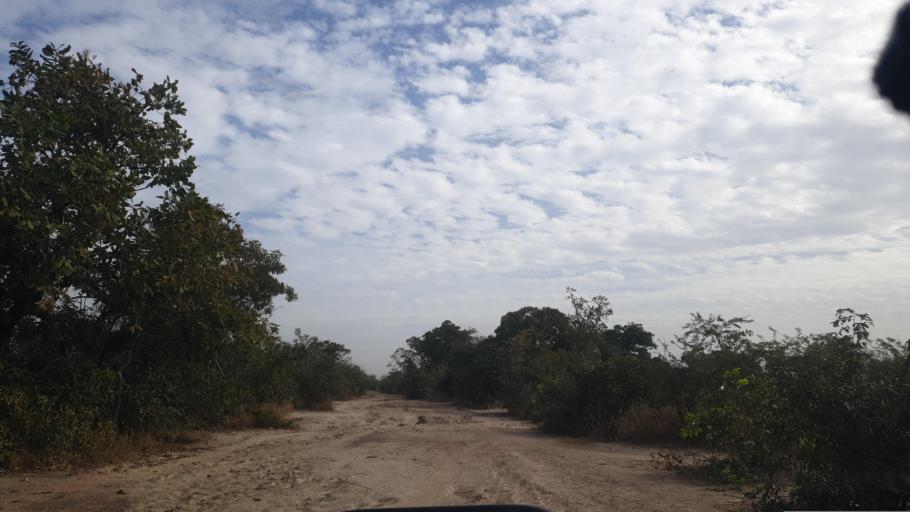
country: ML
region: Sikasso
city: Yanfolila
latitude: 11.4087
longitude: -8.0089
